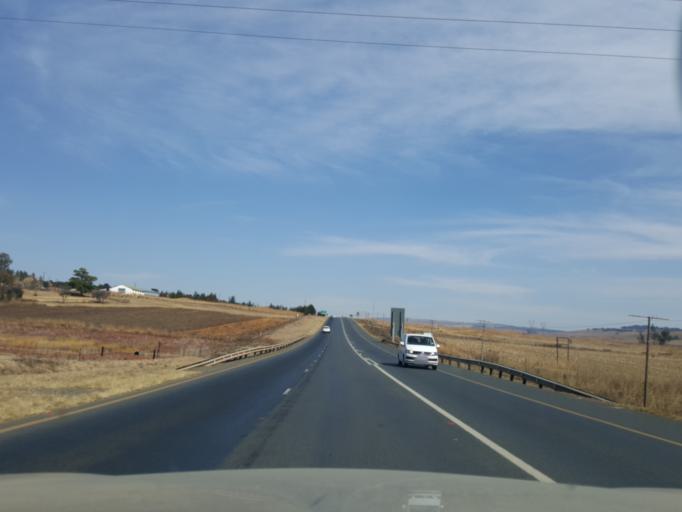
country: ZA
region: Mpumalanga
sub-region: Nkangala District Municipality
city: Belfast
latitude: -25.6738
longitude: 30.2334
